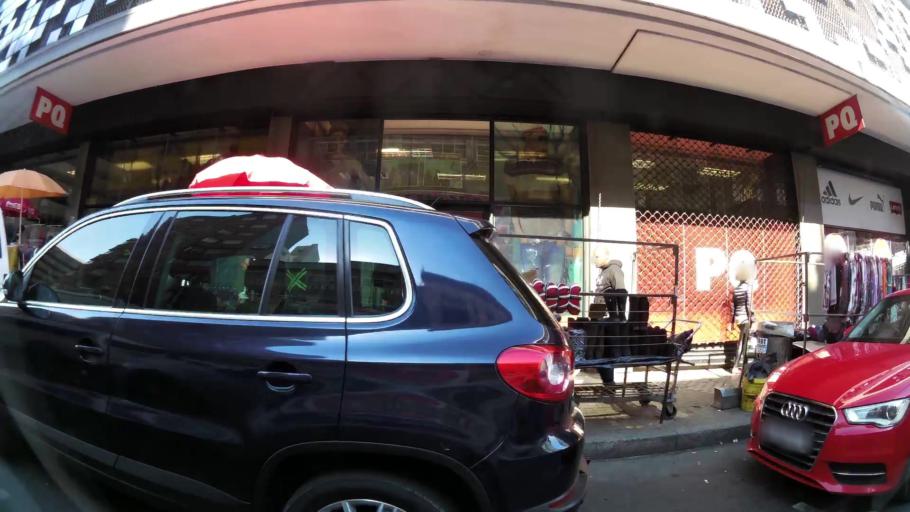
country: ZA
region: Gauteng
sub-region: City of Johannesburg Metropolitan Municipality
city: Johannesburg
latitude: -26.2008
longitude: 28.0429
